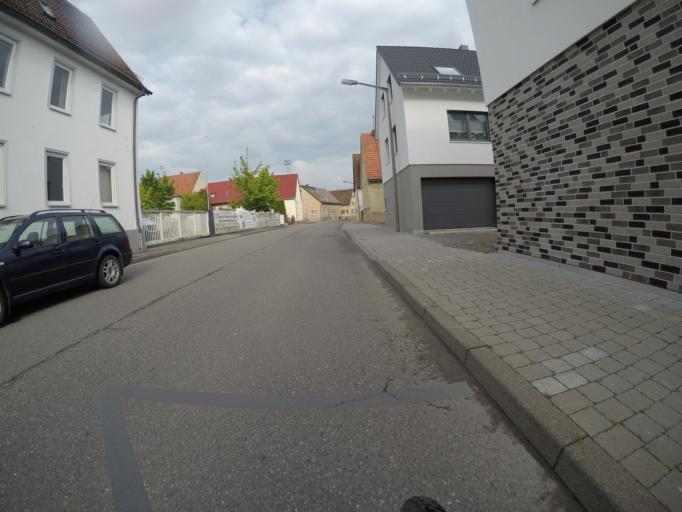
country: DE
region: Baden-Wuerttemberg
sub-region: Regierungsbezirk Stuttgart
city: Magstadt
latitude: 48.7432
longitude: 8.9586
